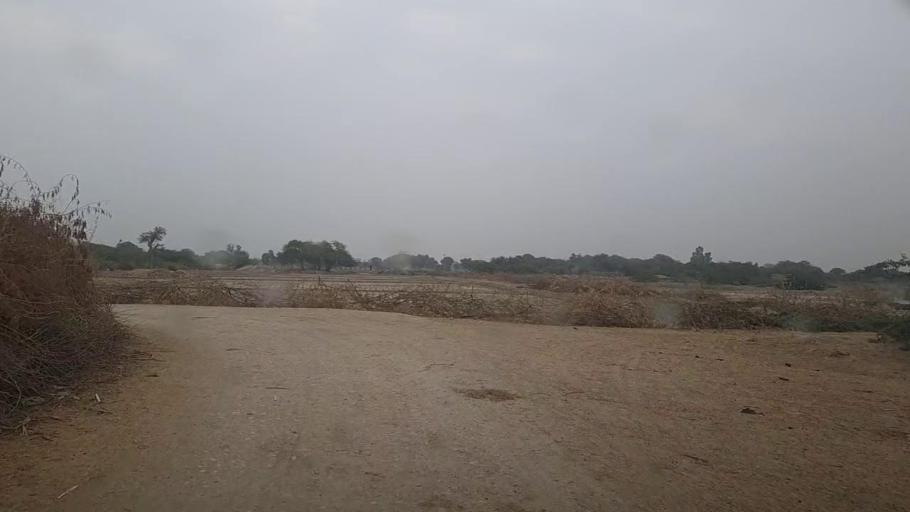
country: PK
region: Sindh
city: Gambat
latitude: 27.3453
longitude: 68.6025
